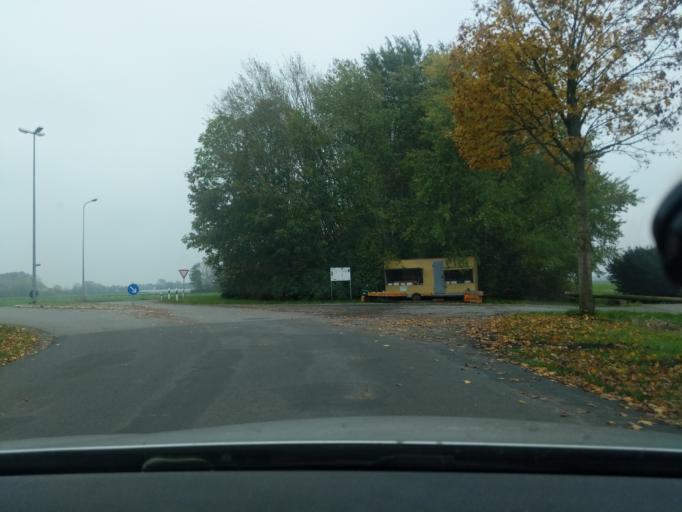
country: DE
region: Lower Saxony
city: Cuxhaven
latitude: 53.8334
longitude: 8.7381
